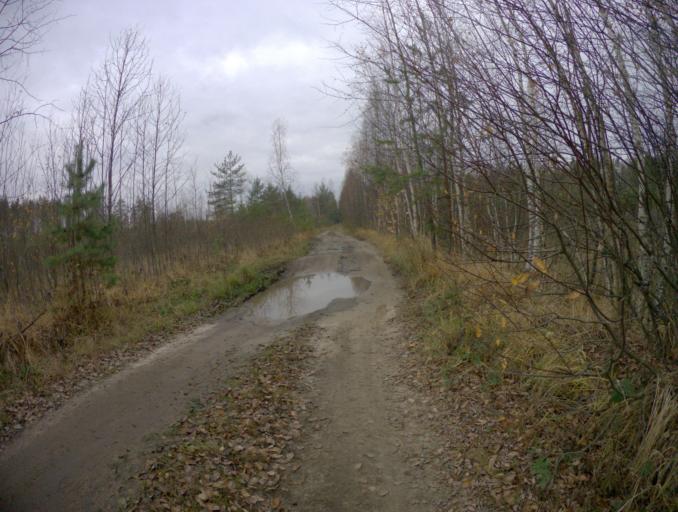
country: RU
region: Moskovskaya
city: Malaya Dubna
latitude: 55.9415
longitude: 38.9813
